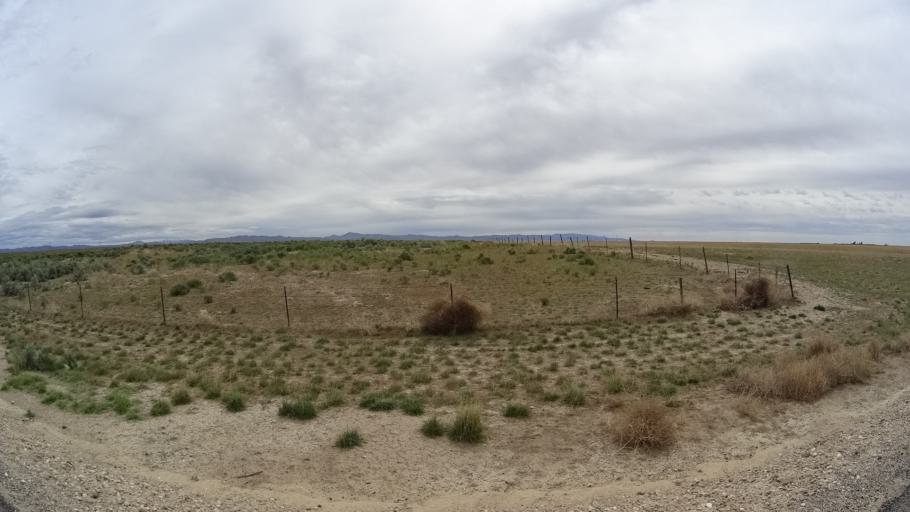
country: US
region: Idaho
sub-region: Ada County
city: Boise
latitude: 43.3578
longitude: -116.0049
